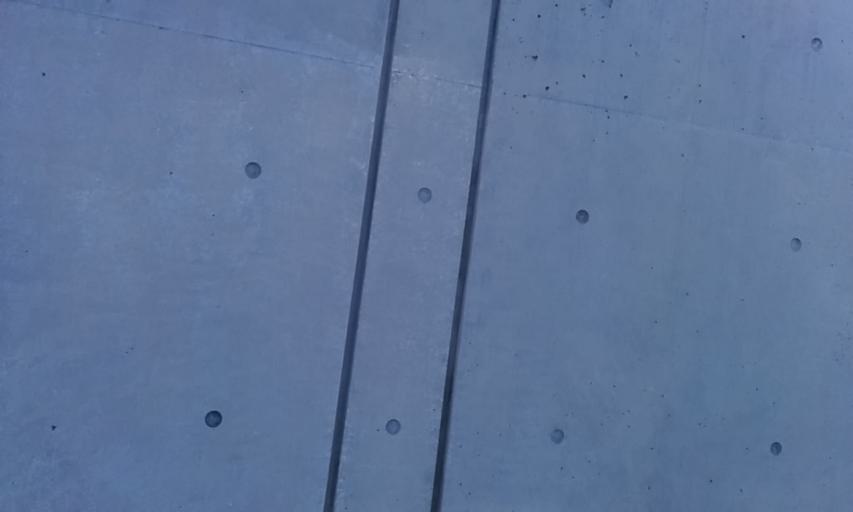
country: JP
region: Tokyo
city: Mitaka-shi
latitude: 35.6615
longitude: 139.5802
